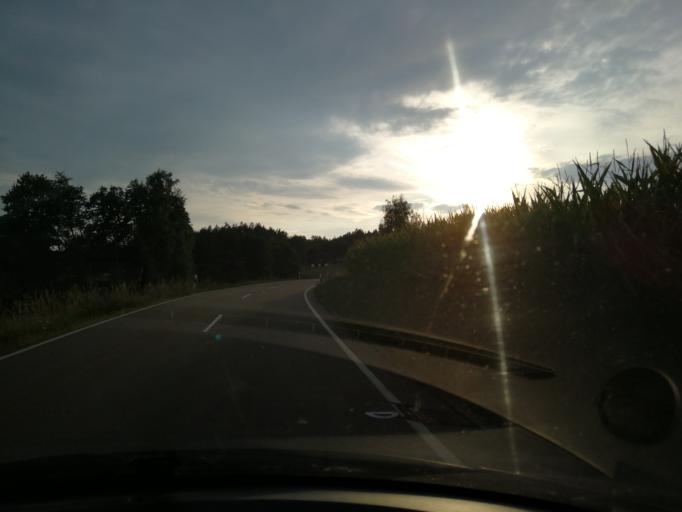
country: DE
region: Bavaria
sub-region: Lower Bavaria
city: Falkenfels
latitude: 49.0428
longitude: 12.6046
